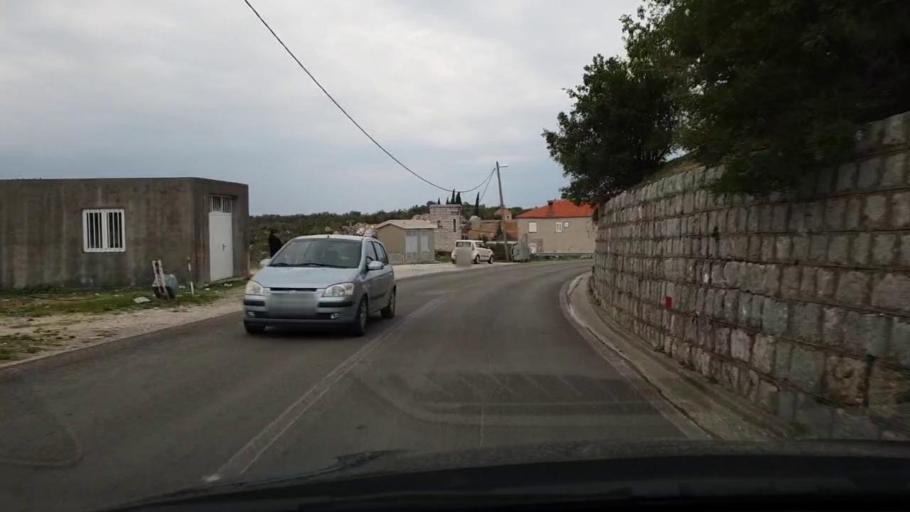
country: HR
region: Dubrovacko-Neretvanska
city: Cibaca
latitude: 42.6458
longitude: 18.1586
